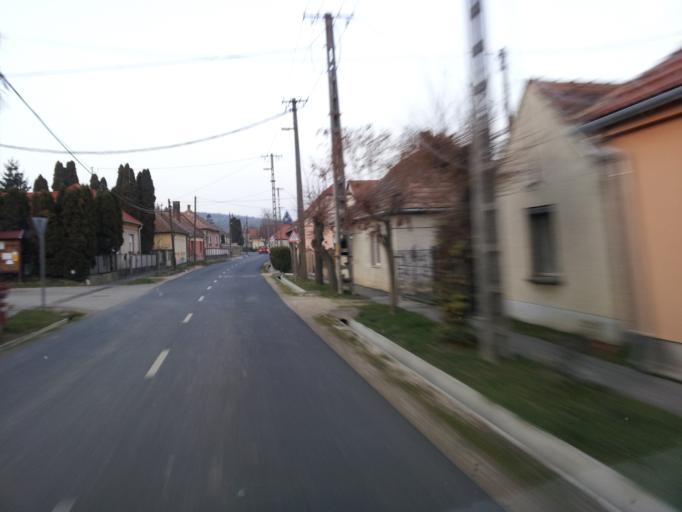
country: HU
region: Zala
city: Zalaszentgrot
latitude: 46.9015
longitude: 17.1529
